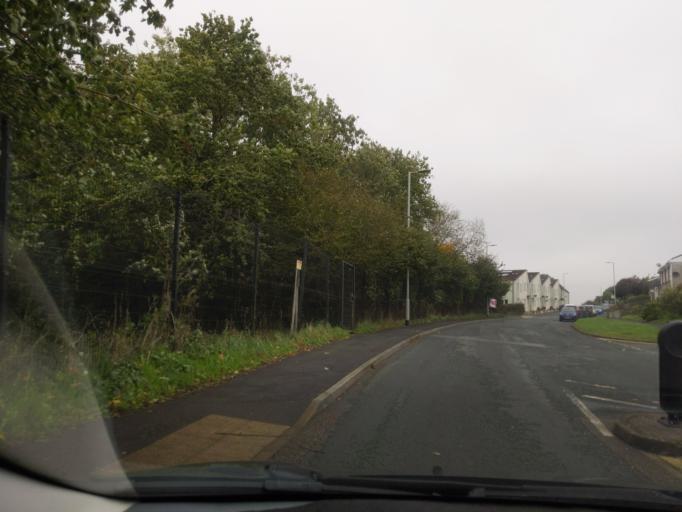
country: GB
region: England
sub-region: Devon
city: Plympton
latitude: 50.4126
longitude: -4.0968
